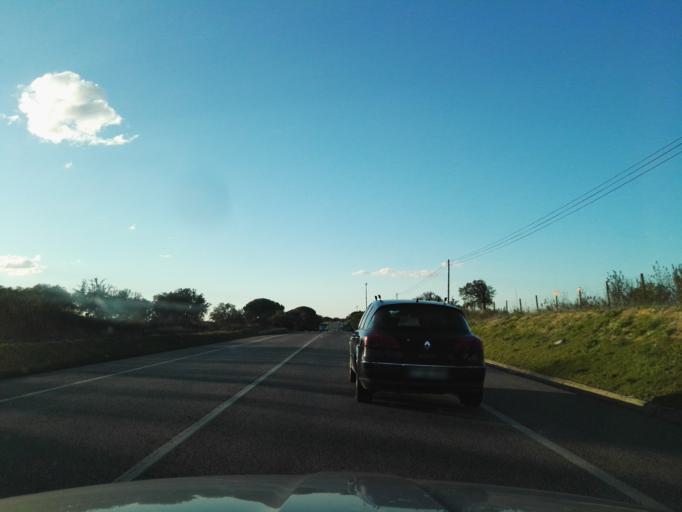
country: PT
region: Santarem
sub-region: Benavente
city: Poceirao
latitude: 38.8404
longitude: -8.7398
